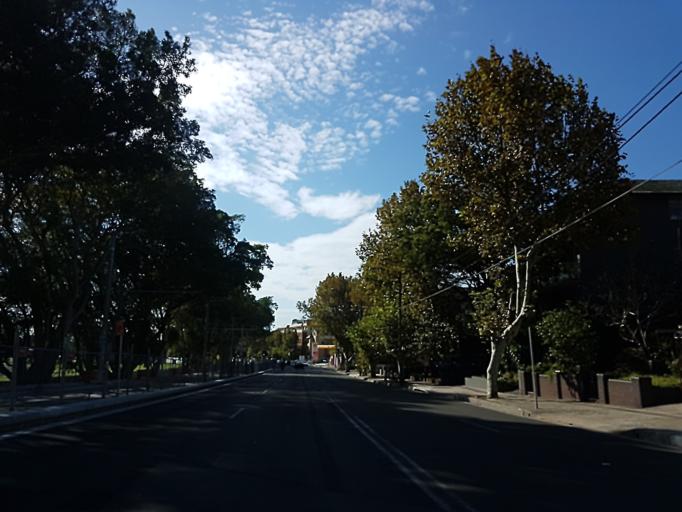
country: AU
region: New South Wales
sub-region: Randwick
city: Randwick
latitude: -33.9095
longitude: 151.2347
